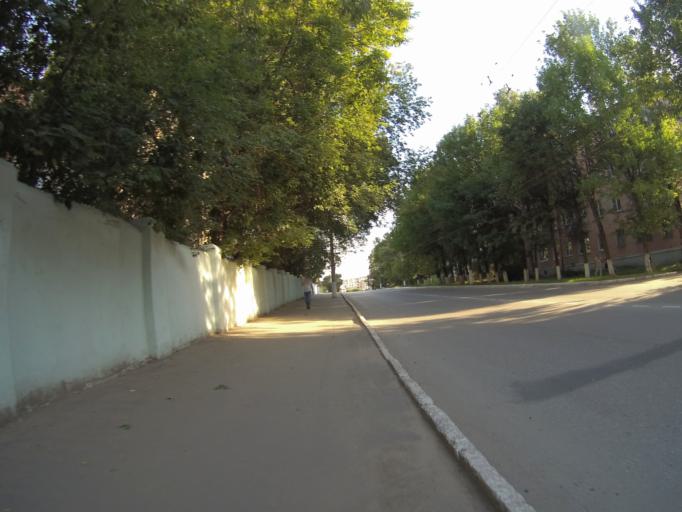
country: RU
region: Vladimir
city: Vladimir
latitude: 56.1412
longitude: 40.4266
